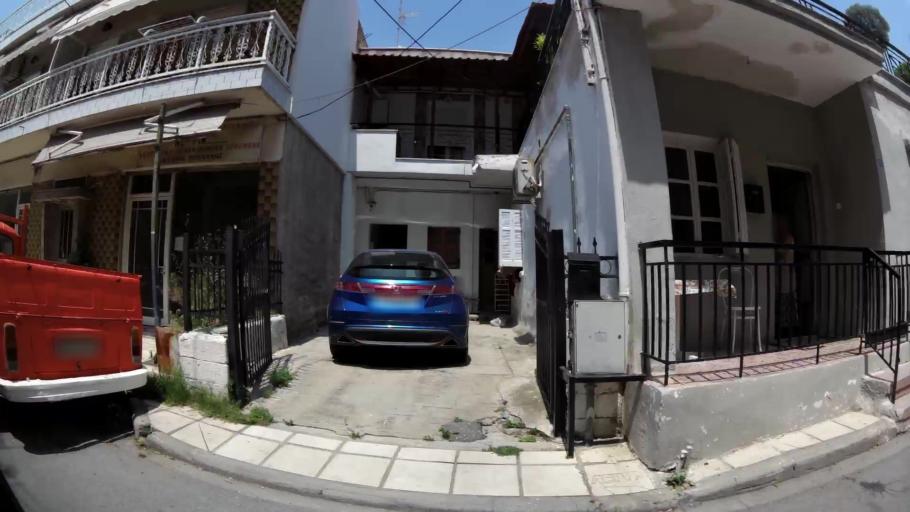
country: GR
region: Central Macedonia
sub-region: Nomos Thessalonikis
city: Evosmos
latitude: 40.6662
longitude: 22.9072
